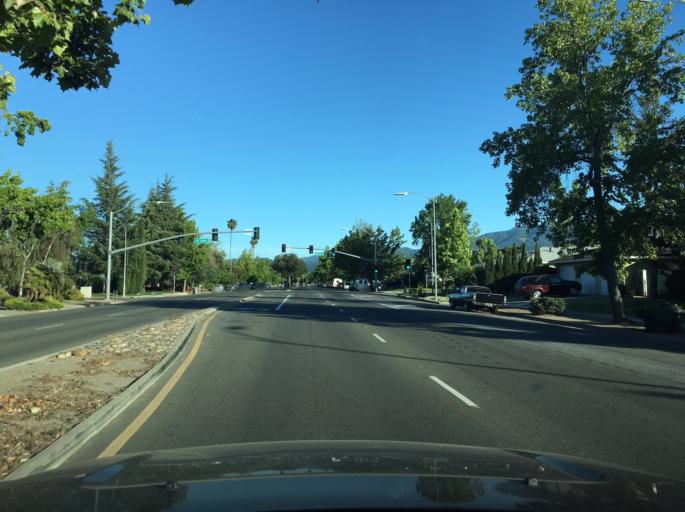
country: US
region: California
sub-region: Santa Clara County
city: Cambrian Park
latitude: 37.2568
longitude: -121.9157
